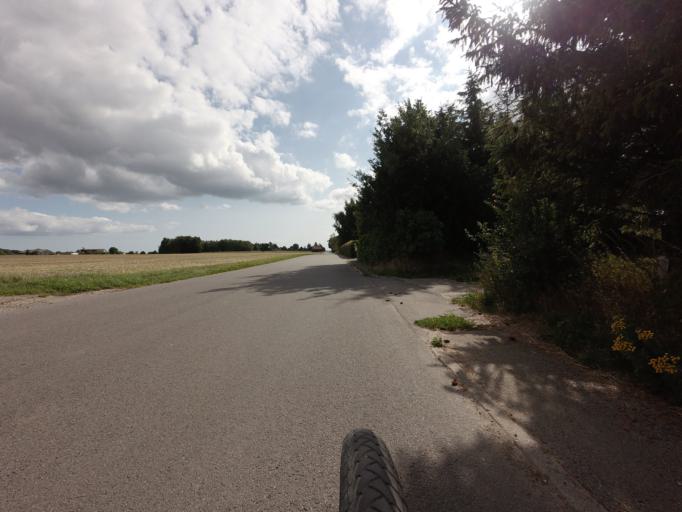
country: DK
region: Zealand
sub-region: Vordingborg Kommune
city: Stege
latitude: 54.9986
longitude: 12.3123
